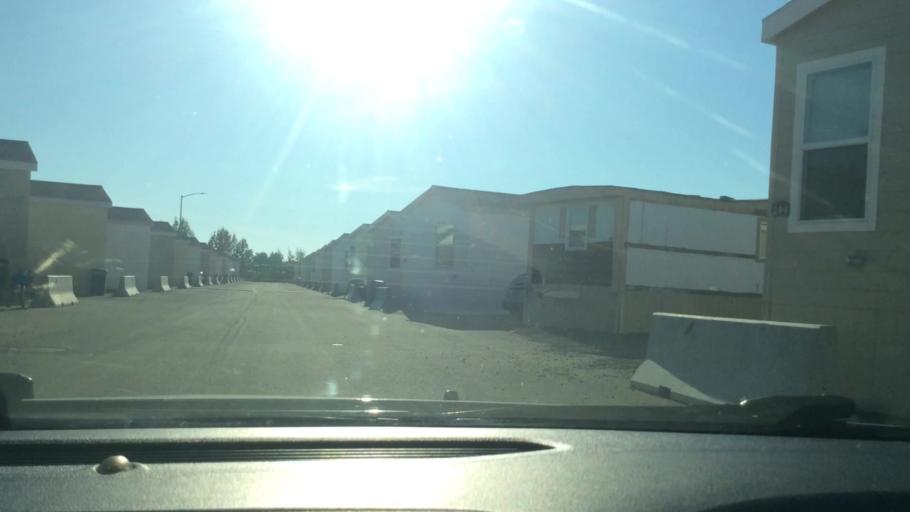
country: US
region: Alaska
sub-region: Anchorage Municipality
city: Anchorage
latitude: 61.2200
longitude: -149.7664
